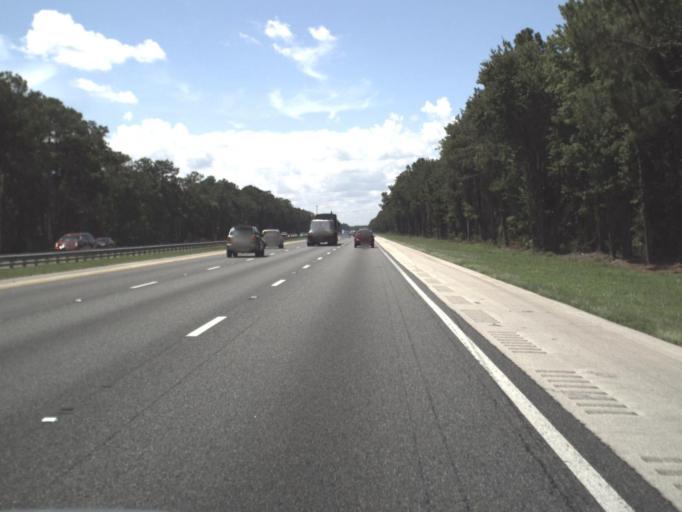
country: US
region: Florida
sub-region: Saint Johns County
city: Saint Augustine
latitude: 29.8786
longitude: -81.4004
